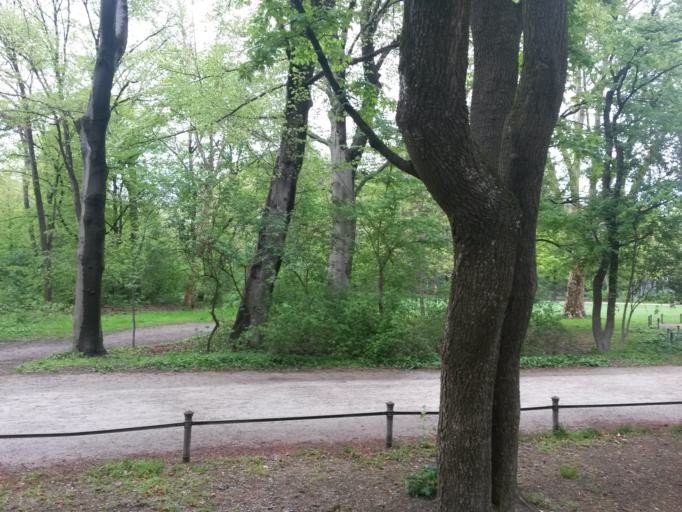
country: DE
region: Bavaria
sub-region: Upper Bavaria
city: Munich
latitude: 48.1438
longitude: 11.5890
